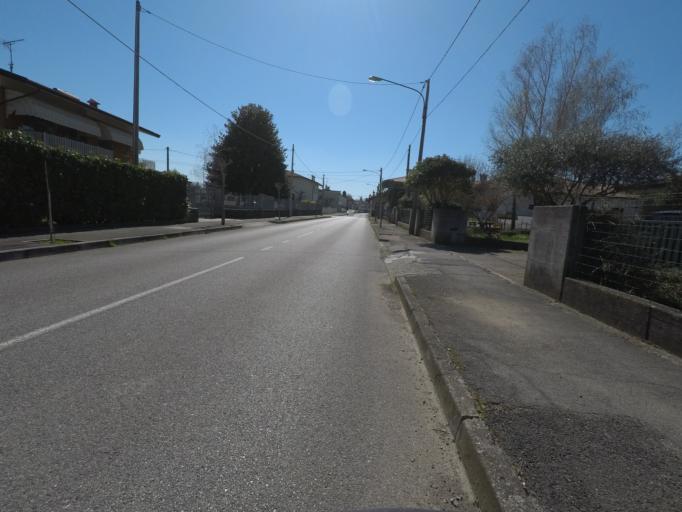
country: IT
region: Friuli Venezia Giulia
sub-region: Provincia di Gorizia
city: Moraro
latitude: 45.9243
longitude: 13.4811
